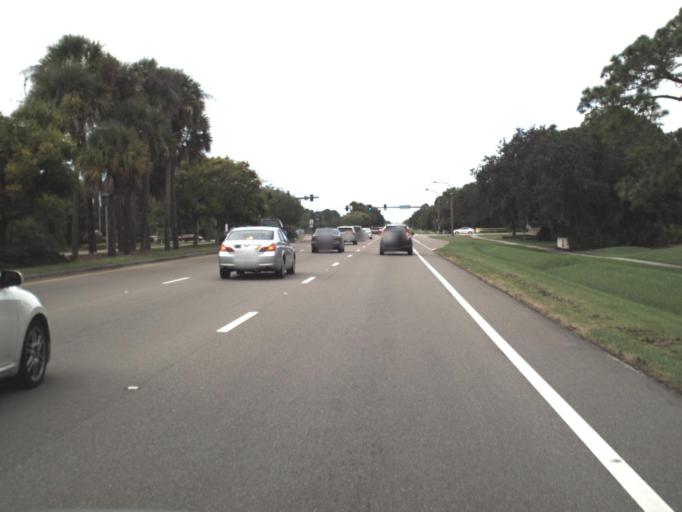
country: US
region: Florida
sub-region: Sarasota County
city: Desoto Lakes
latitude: 27.3885
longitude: -82.4768
